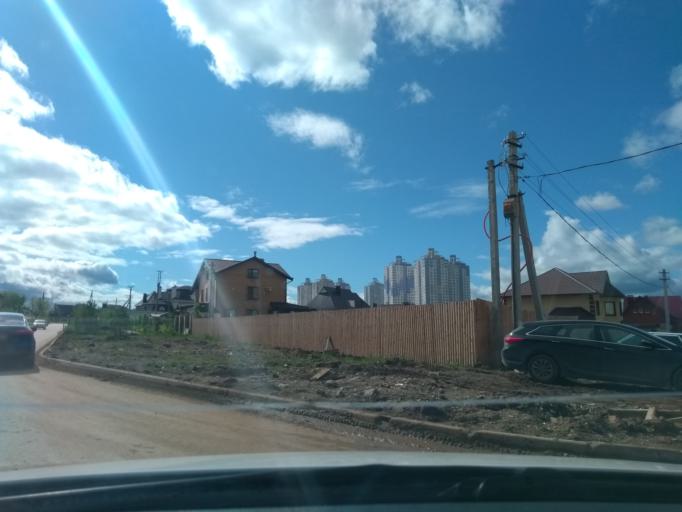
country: RU
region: Perm
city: Perm
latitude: 58.0022
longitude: 56.3325
